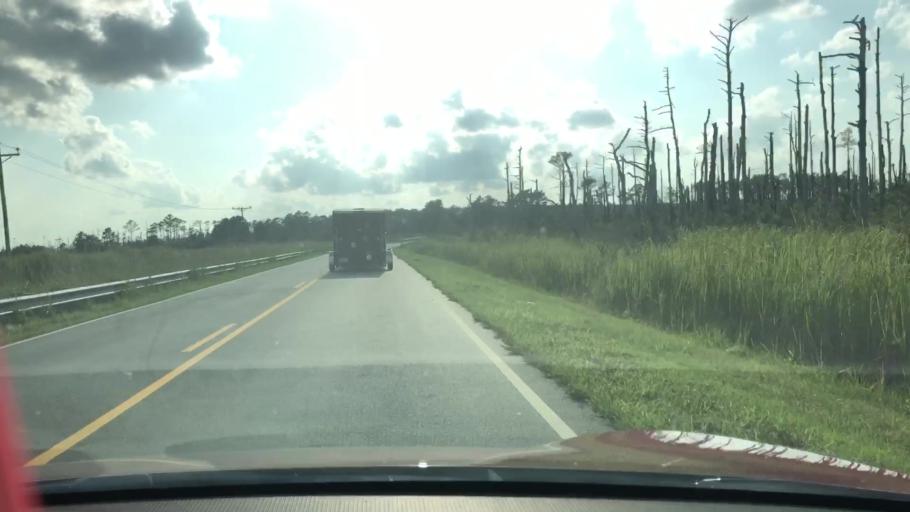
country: US
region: North Carolina
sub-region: Dare County
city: Wanchese
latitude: 35.6076
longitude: -75.8143
